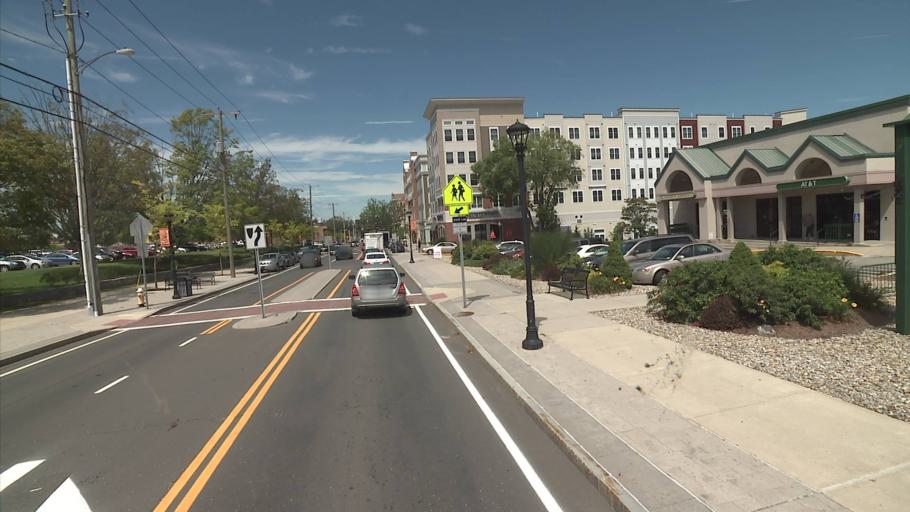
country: US
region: Connecticut
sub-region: Tolland County
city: Storrs
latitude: 41.8031
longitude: -72.2427
